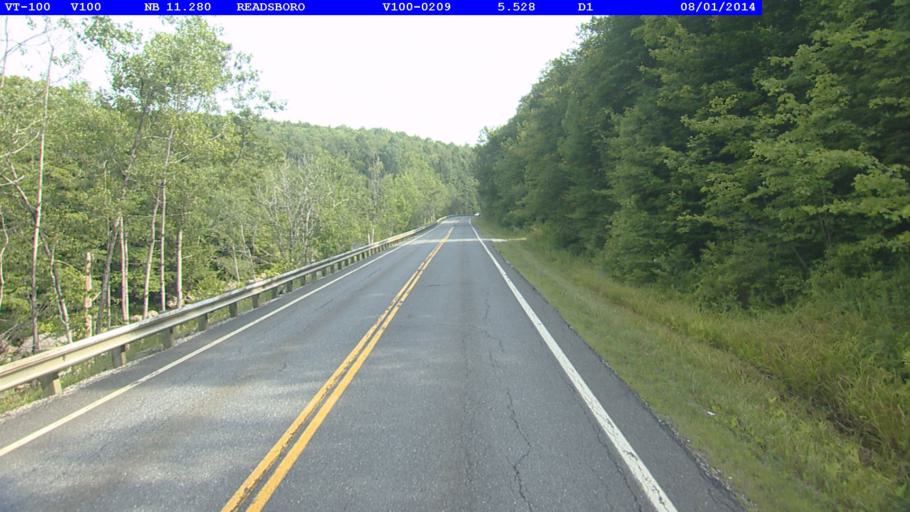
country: US
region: Massachusetts
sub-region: Berkshire County
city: North Adams
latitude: 42.7876
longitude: -72.9610
